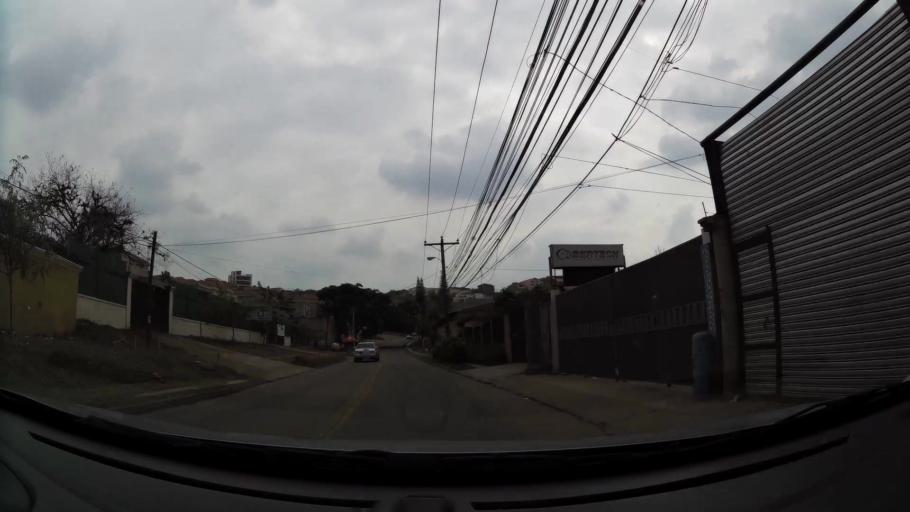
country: HN
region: Francisco Morazan
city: Tegucigalpa
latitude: 14.0907
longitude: -87.1719
